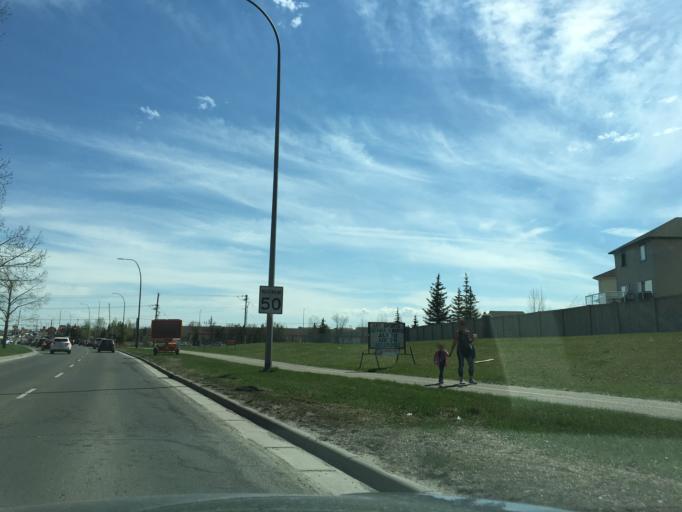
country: CA
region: Alberta
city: Calgary
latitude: 50.9028
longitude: -114.0726
